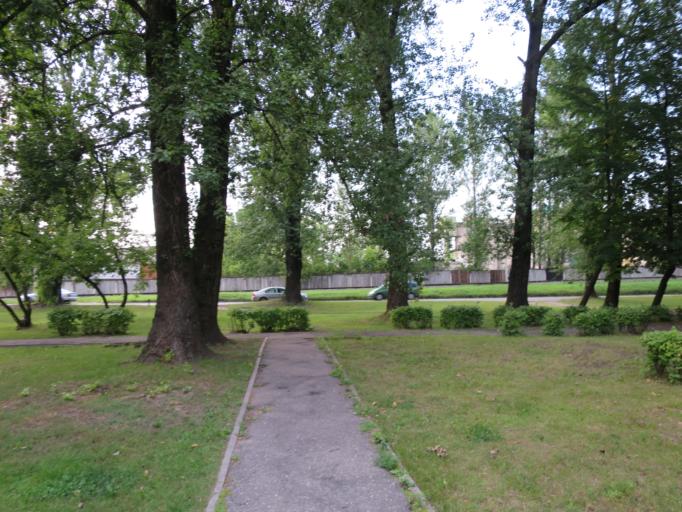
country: LV
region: Riga
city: Riga
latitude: 56.9749
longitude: 24.1062
